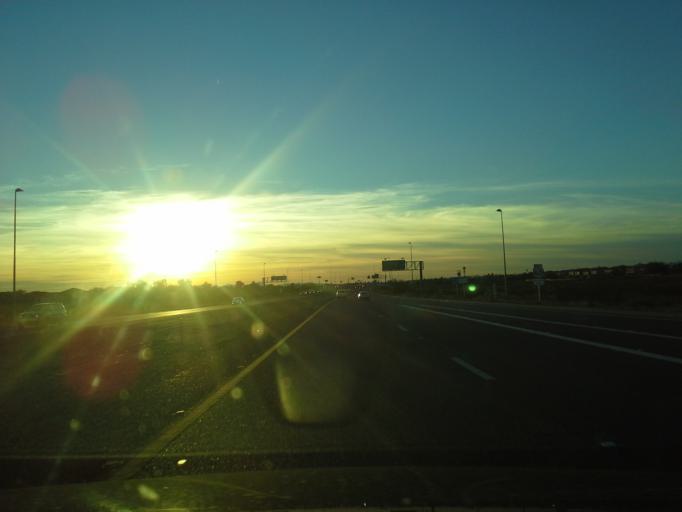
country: US
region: Arizona
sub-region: Pinal County
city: Apache Junction
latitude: 33.3868
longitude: -111.5176
